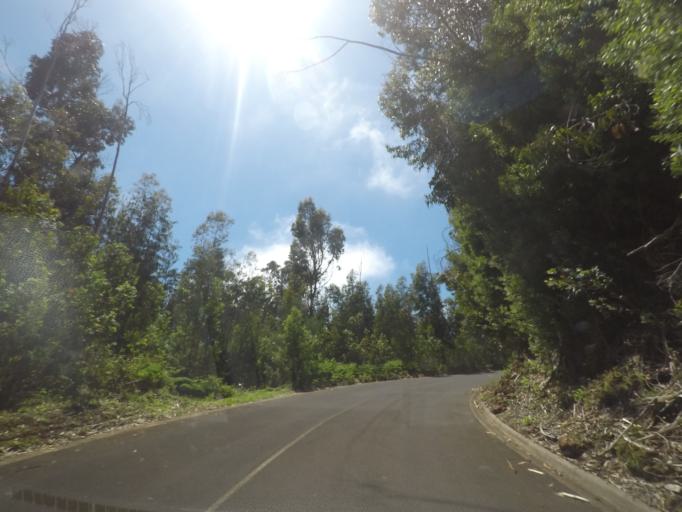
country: PT
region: Madeira
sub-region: Calheta
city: Arco da Calheta
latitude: 32.7358
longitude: -17.1320
